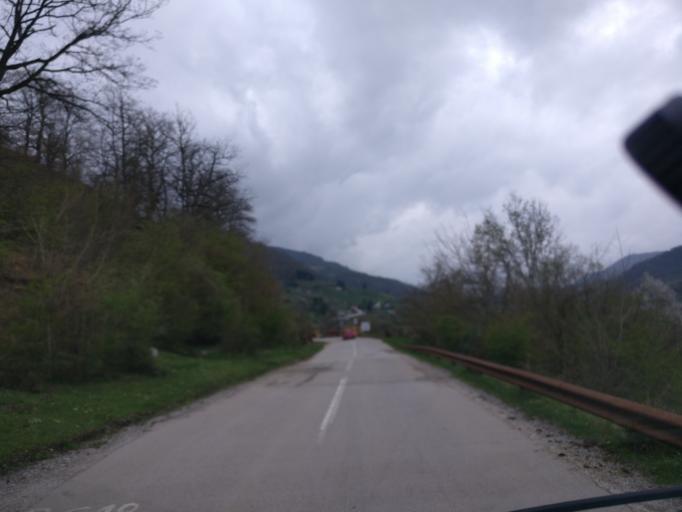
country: BA
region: Republika Srpska
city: Foca
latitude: 43.4414
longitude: 18.7602
